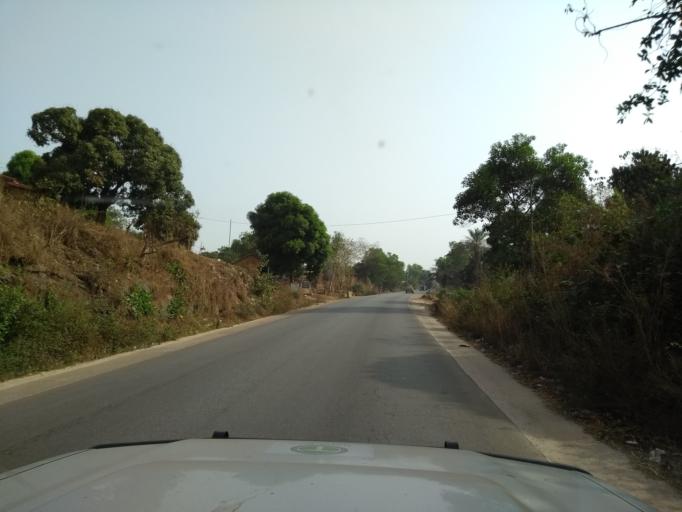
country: GN
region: Kindia
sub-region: Prefecture de Dubreka
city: Dubreka
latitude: 9.8459
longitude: -13.4866
